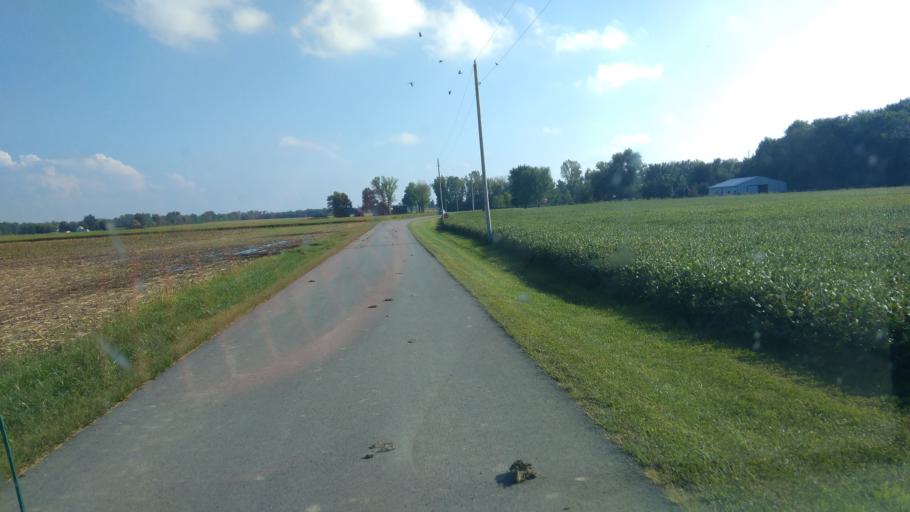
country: US
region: Ohio
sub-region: Hardin County
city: Forest
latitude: 40.7321
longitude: -83.4776
